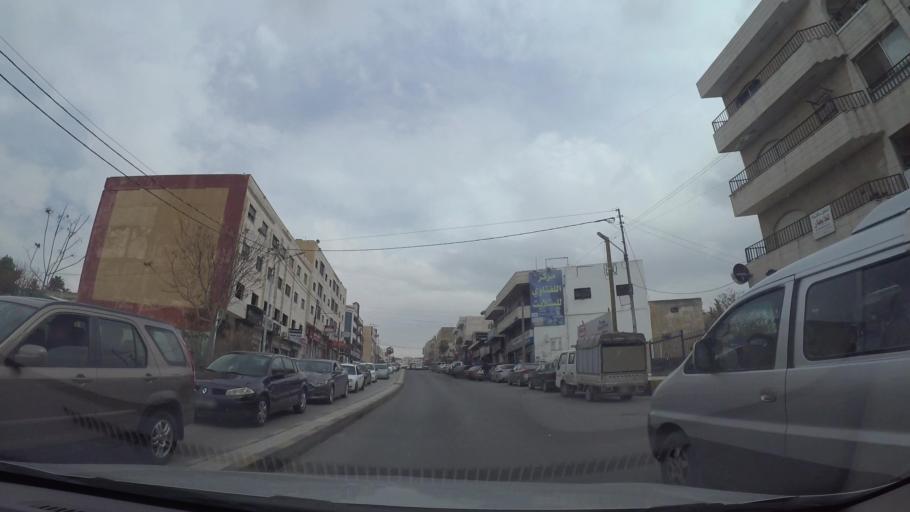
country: JO
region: Amman
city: Umm as Summaq
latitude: 31.8877
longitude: 35.8527
